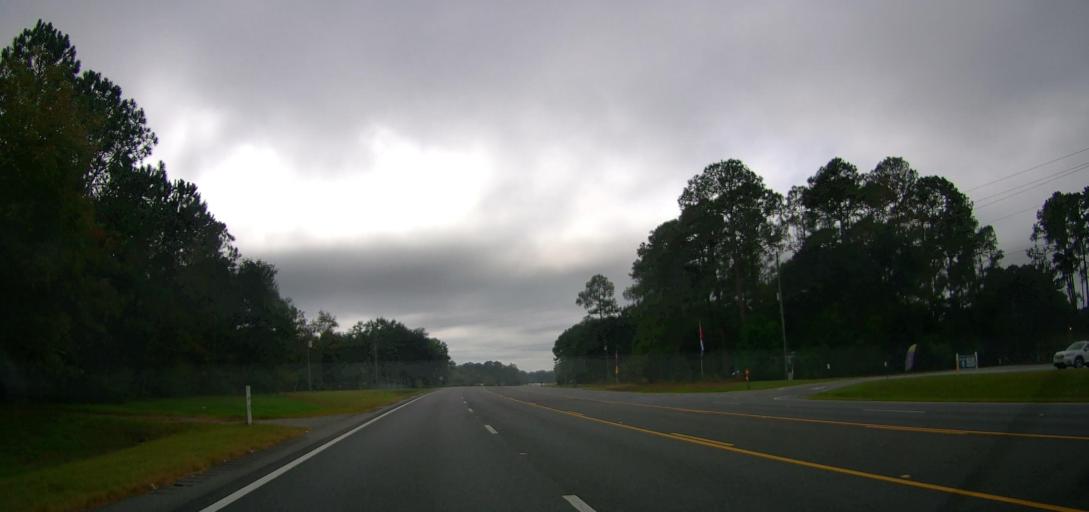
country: US
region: Georgia
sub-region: Thomas County
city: Thomasville
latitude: 30.9864
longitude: -83.8786
